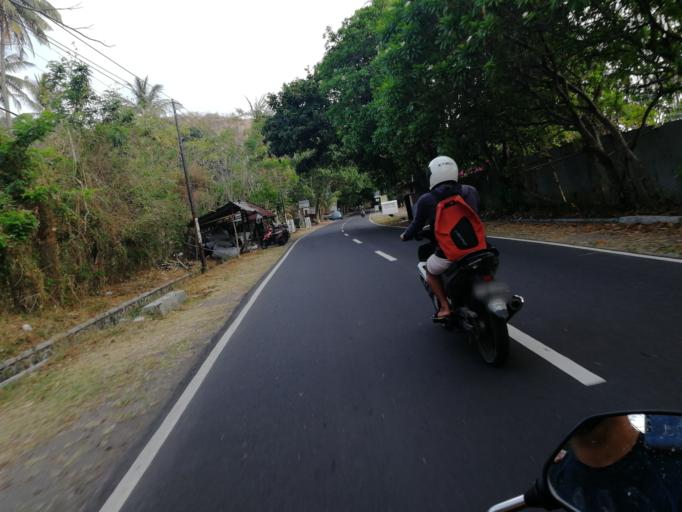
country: ID
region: West Nusa Tenggara
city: Karangsubagan
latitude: -8.4567
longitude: 116.0391
